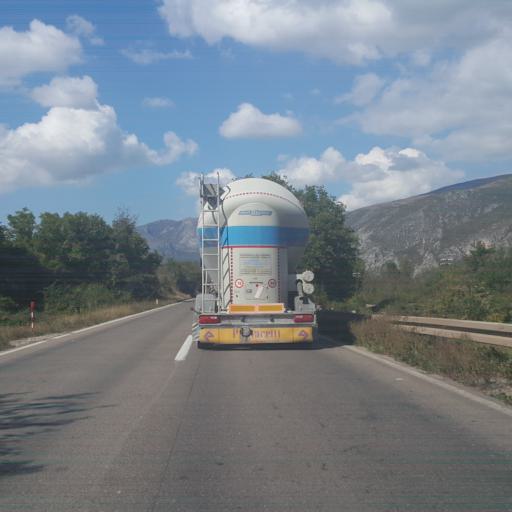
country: RS
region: Central Serbia
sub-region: Pirotski Okrug
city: Bela Palanka
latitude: 43.2815
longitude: 22.2223
